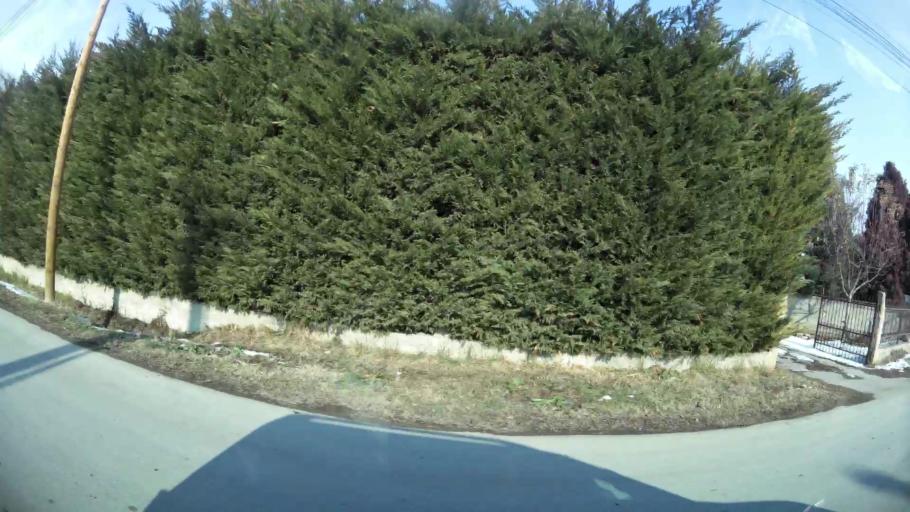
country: MK
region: Suto Orizari
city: Suto Orizare
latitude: 42.0255
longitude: 21.3765
